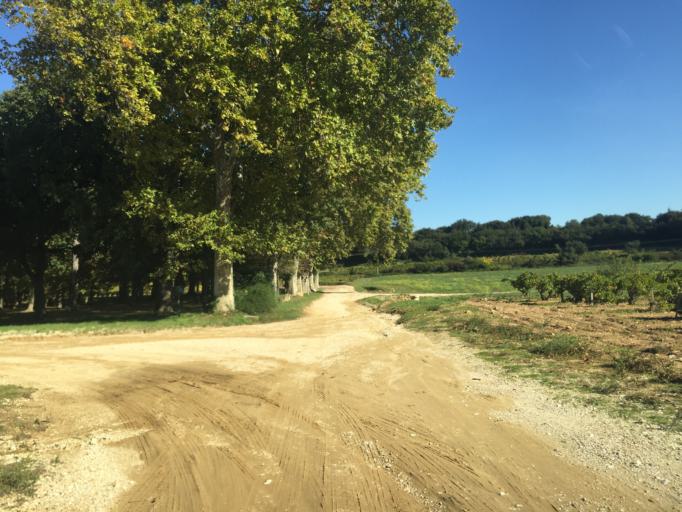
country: FR
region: Provence-Alpes-Cote d'Azur
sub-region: Departement du Vaucluse
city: Chateauneuf-du-Pape
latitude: 44.0683
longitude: 4.8440
